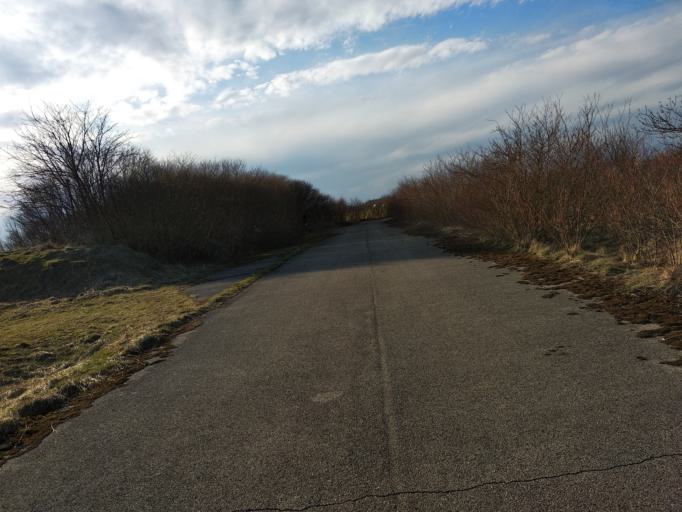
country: DE
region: Bavaria
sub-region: Upper Bavaria
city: Neubiberg
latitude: 48.0694
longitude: 11.6400
